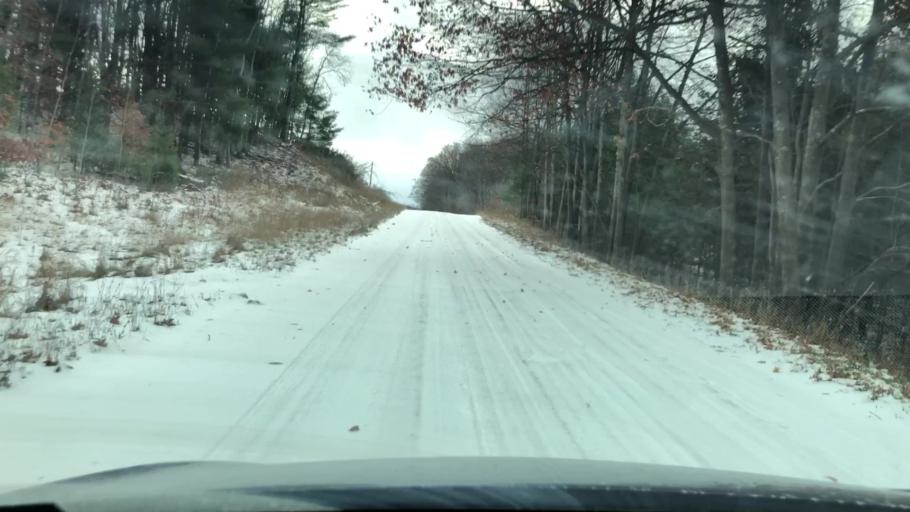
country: US
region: Michigan
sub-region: Antrim County
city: Elk Rapids
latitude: 44.9557
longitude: -85.5155
